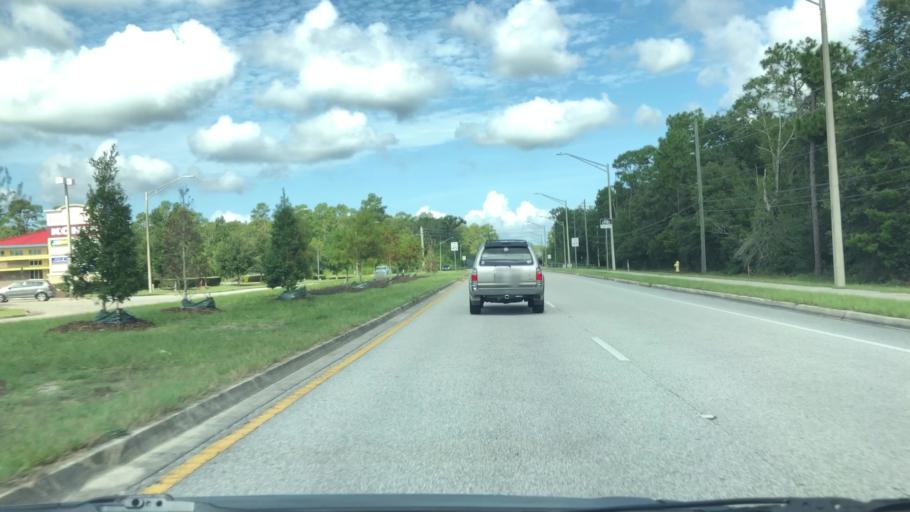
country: US
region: Florida
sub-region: Saint Johns County
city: Fruit Cove
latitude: 30.1429
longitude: -81.5518
